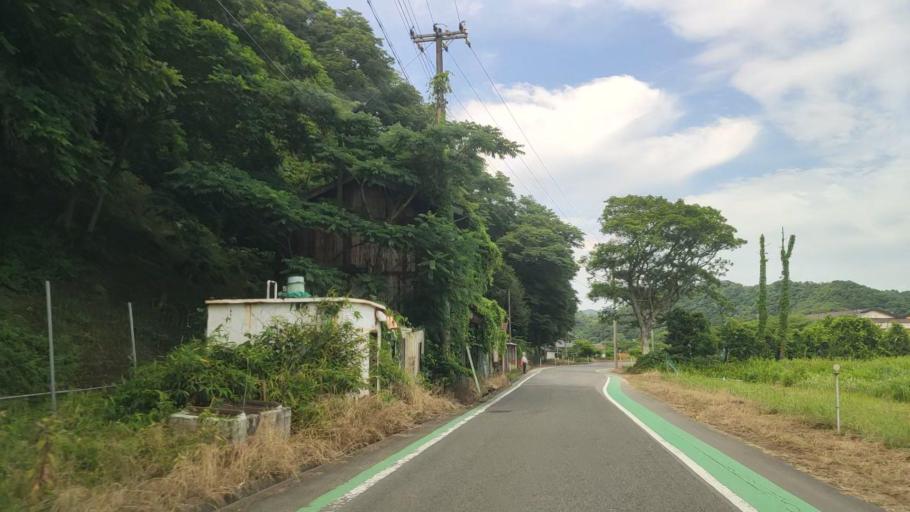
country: JP
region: Hyogo
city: Toyooka
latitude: 35.6417
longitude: 134.8417
